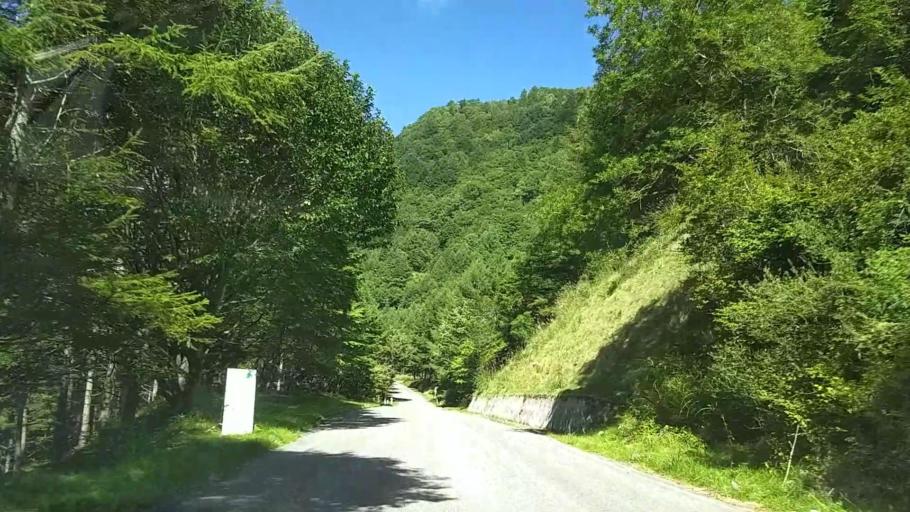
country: JP
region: Nagano
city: Suwa
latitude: 36.1940
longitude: 138.1238
